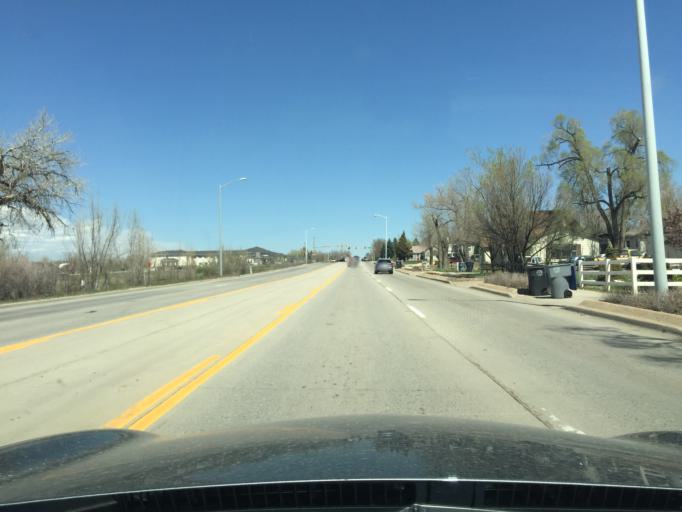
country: US
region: Colorado
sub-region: Boulder County
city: Longmont
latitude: 40.1719
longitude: -105.1308
